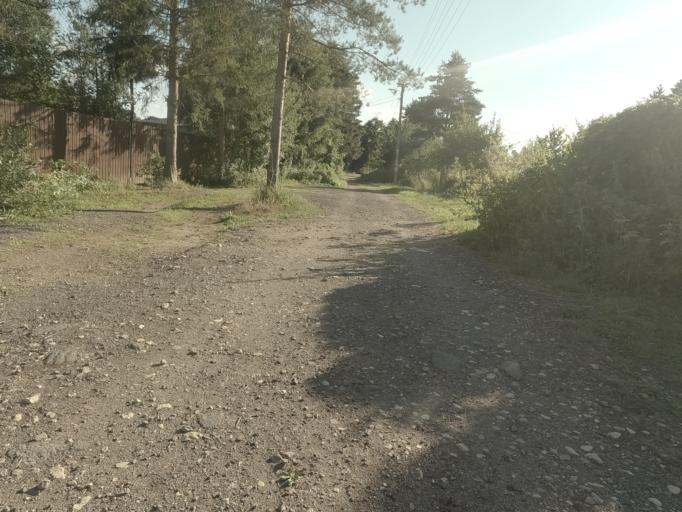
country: RU
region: Leningrad
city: Kirovsk
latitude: 59.9262
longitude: 30.9797
